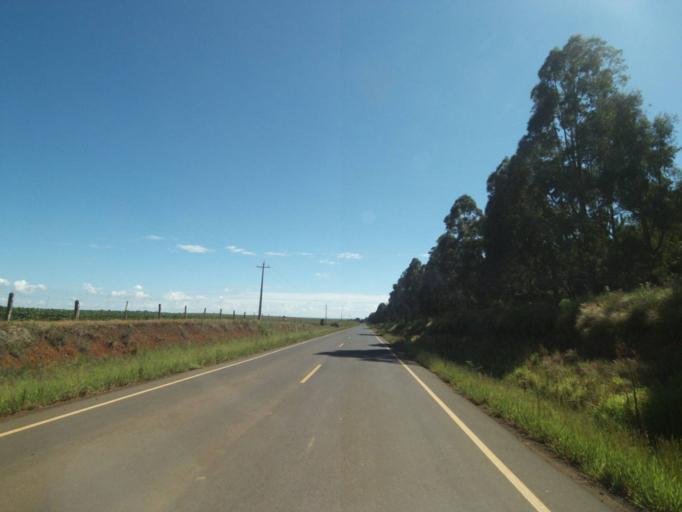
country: BR
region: Parana
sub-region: Pinhao
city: Pinhao
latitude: -25.8281
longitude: -52.0181
